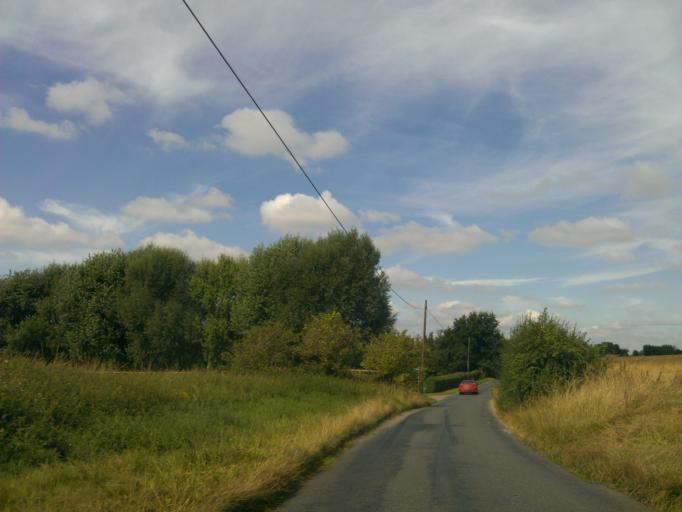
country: GB
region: England
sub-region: Essex
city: Sible Hedingham
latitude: 51.9818
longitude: 0.6023
